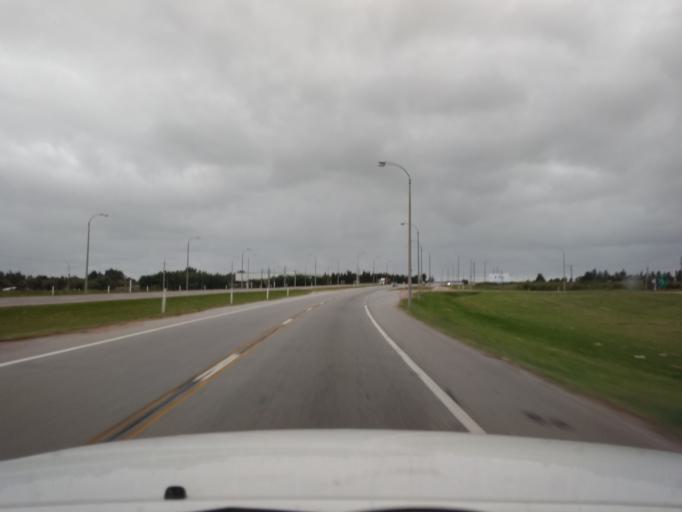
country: UY
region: Canelones
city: Progreso
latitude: -34.6938
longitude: -56.2385
